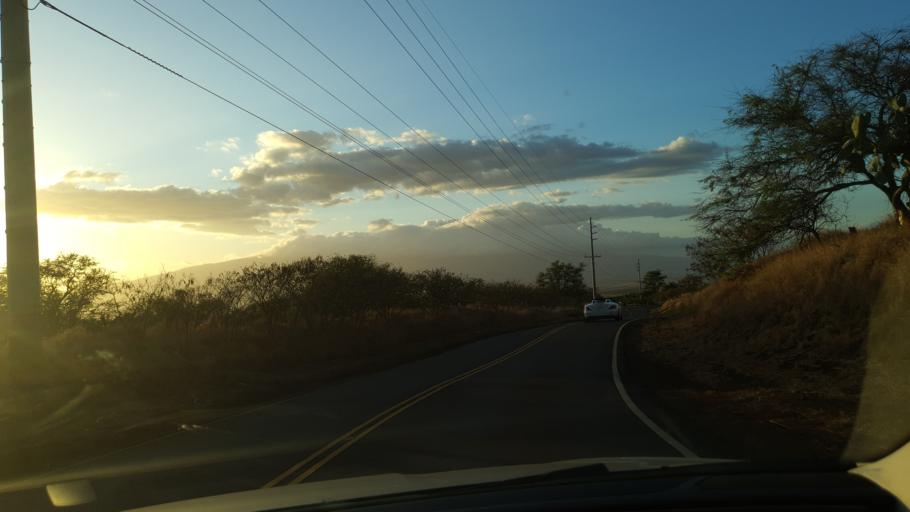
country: US
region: Hawaii
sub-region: Maui County
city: Pukalani
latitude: 20.7927
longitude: -156.3628
